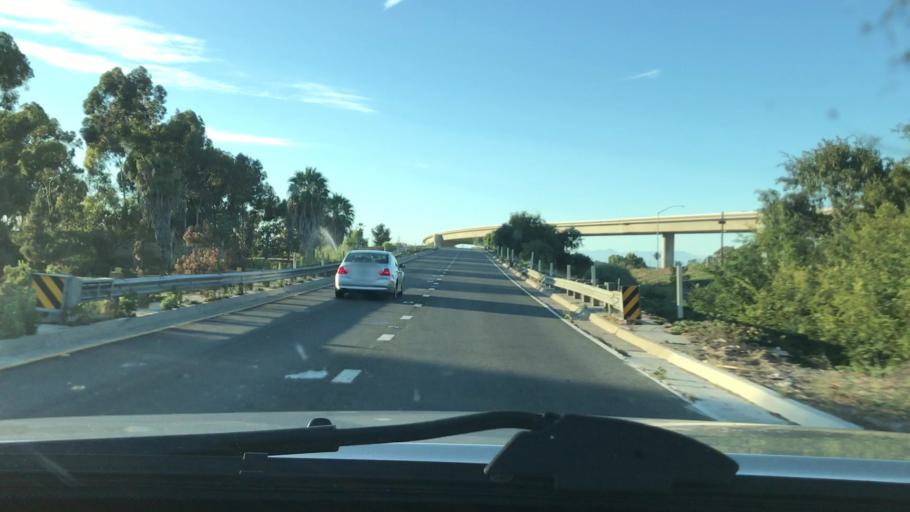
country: US
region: California
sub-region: Orange County
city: Rossmoor
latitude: 33.7768
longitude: -118.0904
